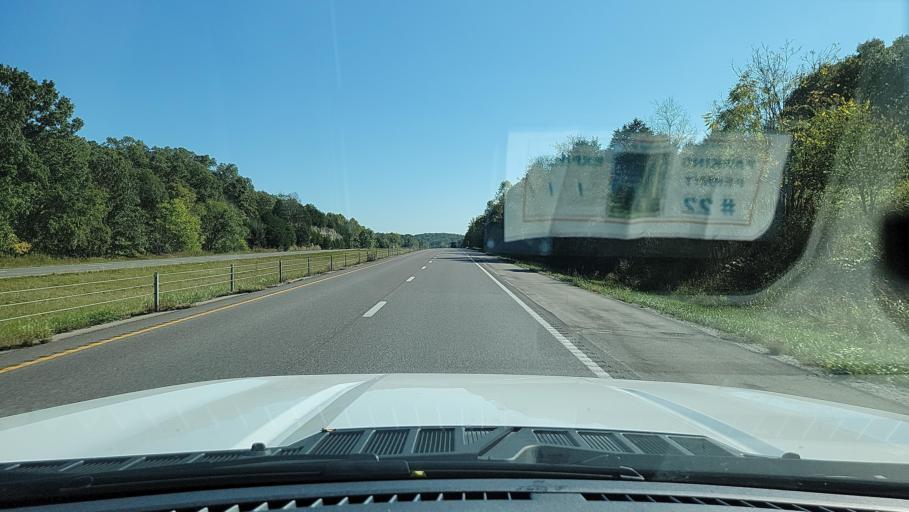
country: US
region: Missouri
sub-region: Jefferson County
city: Crystal City
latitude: 38.0837
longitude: -90.2974
